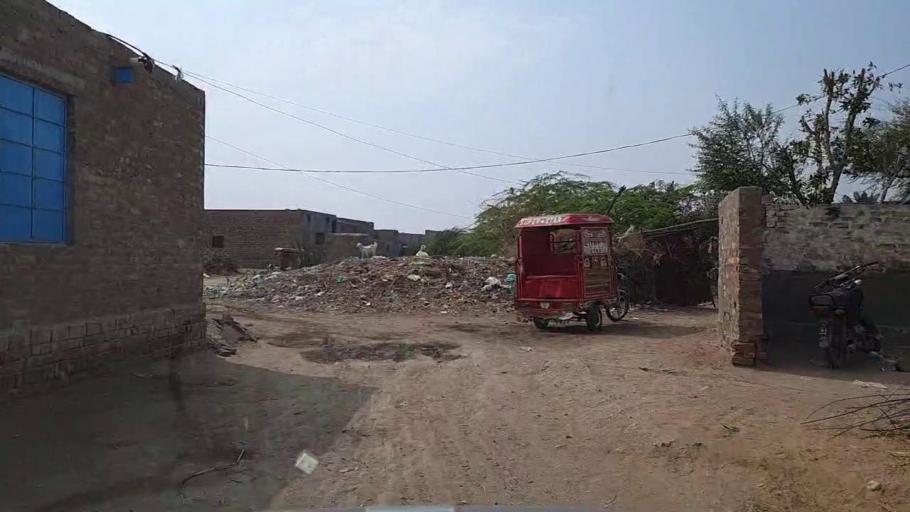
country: PK
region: Sindh
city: Mirwah Gorchani
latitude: 25.3288
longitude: 69.0322
